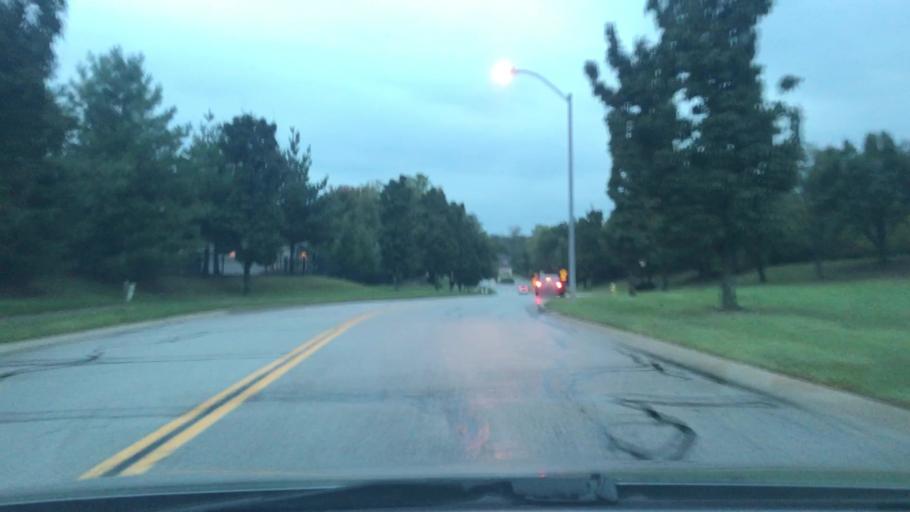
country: US
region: Missouri
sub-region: Jackson County
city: Blue Springs
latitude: 38.9971
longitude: -94.3585
